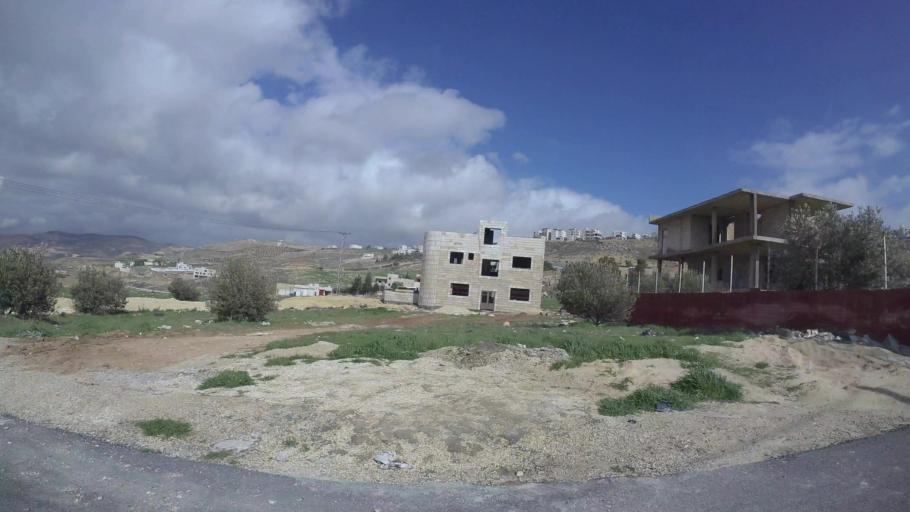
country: JO
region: Amman
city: Al Jubayhah
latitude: 32.0708
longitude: 35.8716
